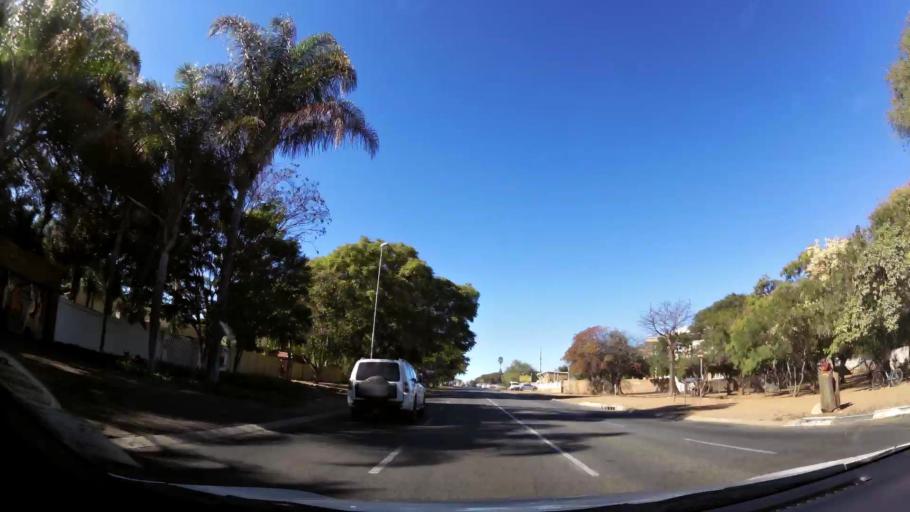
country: ZA
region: Limpopo
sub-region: Capricorn District Municipality
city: Polokwane
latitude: -23.8969
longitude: 29.4684
